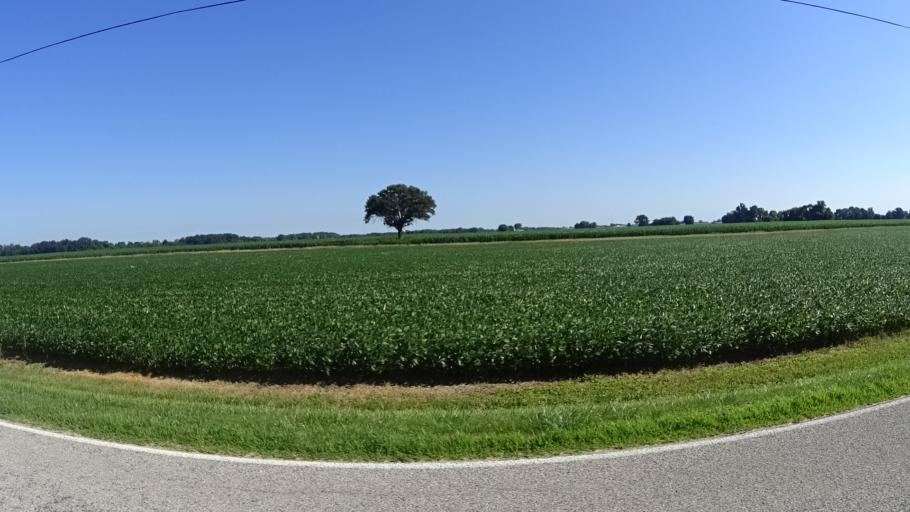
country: US
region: Ohio
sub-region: Erie County
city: Huron
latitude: 41.3771
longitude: -82.6023
